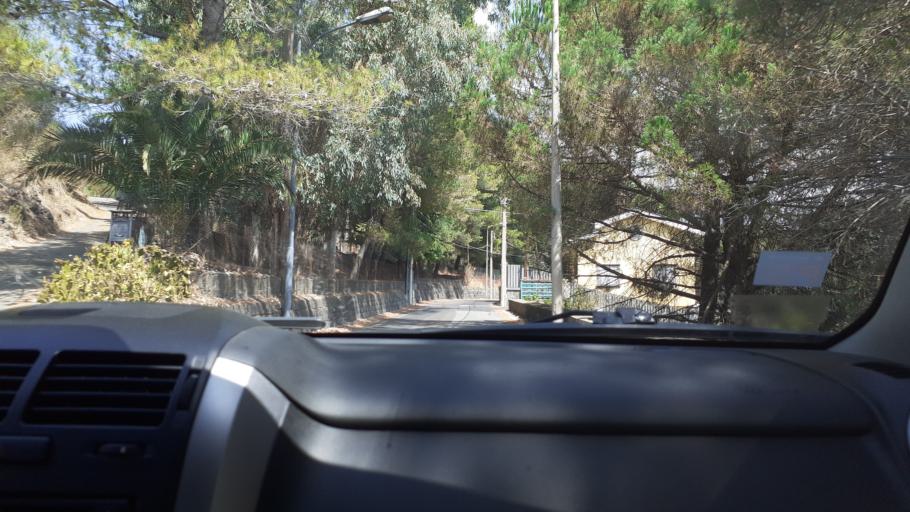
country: IT
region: Sicily
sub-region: Catania
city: Nicolosi
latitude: 37.6249
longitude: 15.0249
